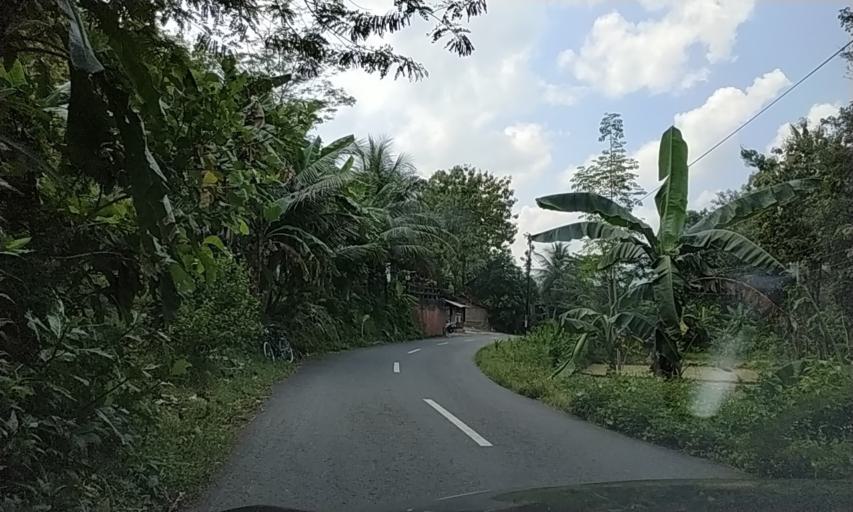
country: ID
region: Central Java
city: Gombong
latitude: -7.6327
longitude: 109.7138
